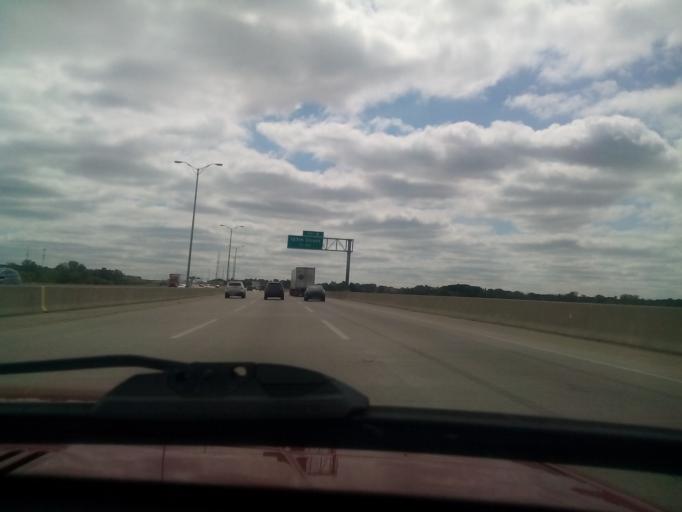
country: US
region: Illinois
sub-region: Cook County
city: Lemont
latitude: 41.6692
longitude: -88.0282
